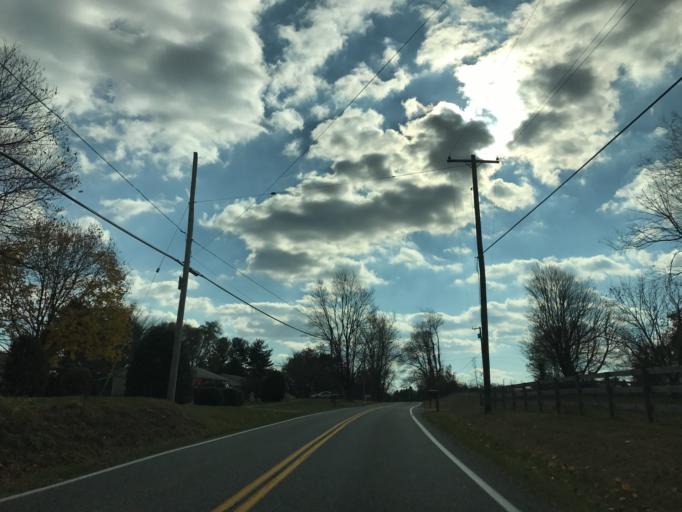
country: US
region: Maryland
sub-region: Harford County
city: Pleasant Hills
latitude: 39.4875
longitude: -76.3743
